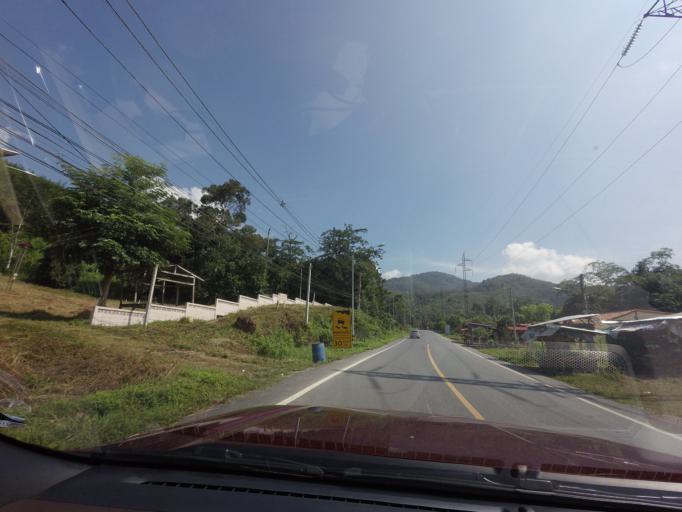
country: TH
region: Yala
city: Betong
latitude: 5.9186
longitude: 101.1684
